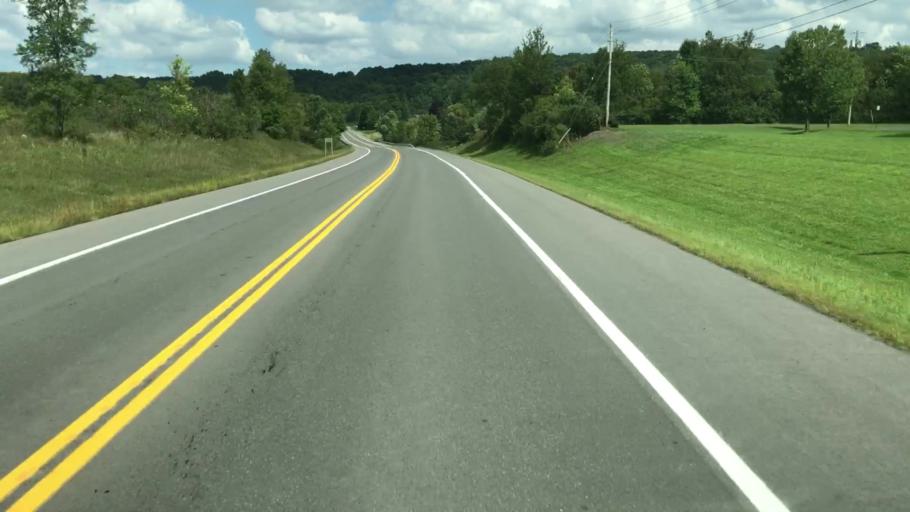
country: US
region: New York
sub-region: Onondaga County
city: Marcellus
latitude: 42.9548
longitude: -76.3440
